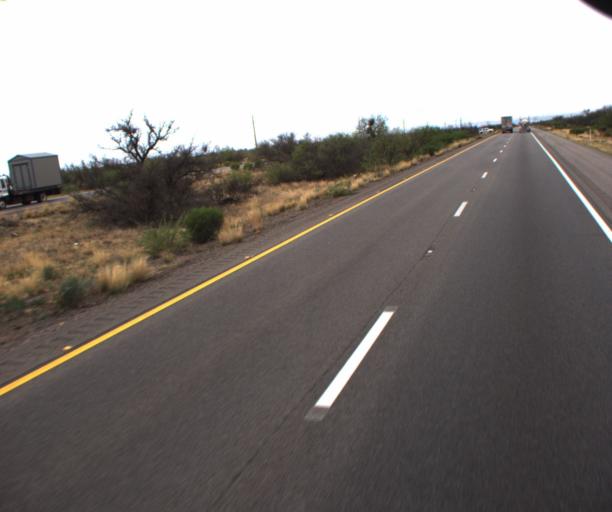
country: US
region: Arizona
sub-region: Cochise County
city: Saint David
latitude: 32.0049
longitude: -110.1432
